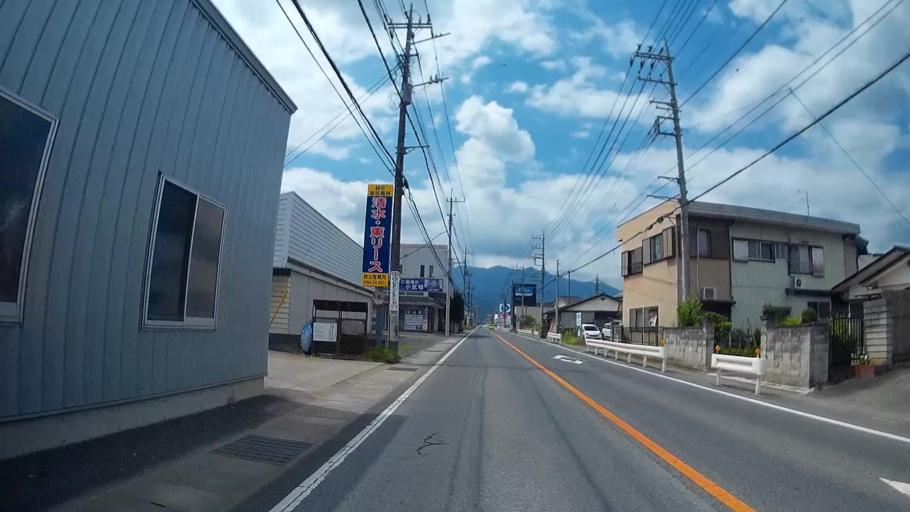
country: JP
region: Saitama
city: Chichibu
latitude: 35.9811
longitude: 139.0766
